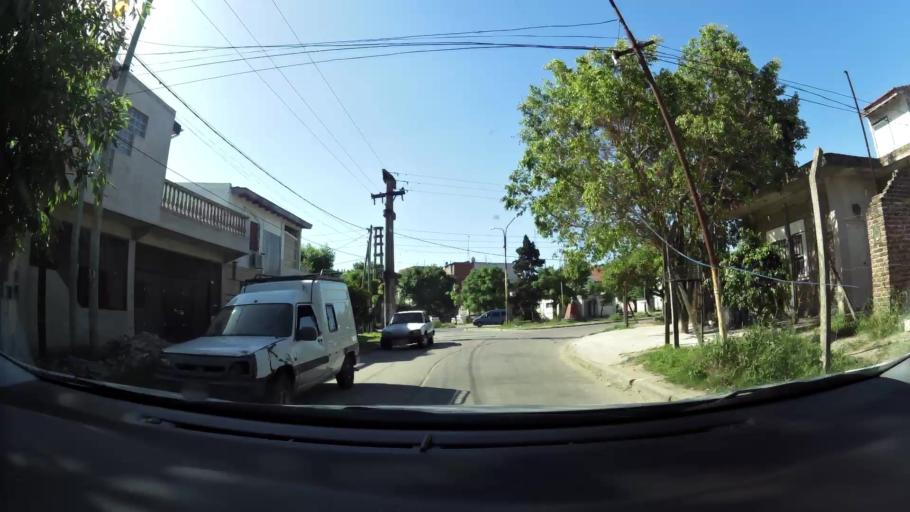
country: AR
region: Buenos Aires F.D.
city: Villa Lugano
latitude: -34.7048
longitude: -58.4769
